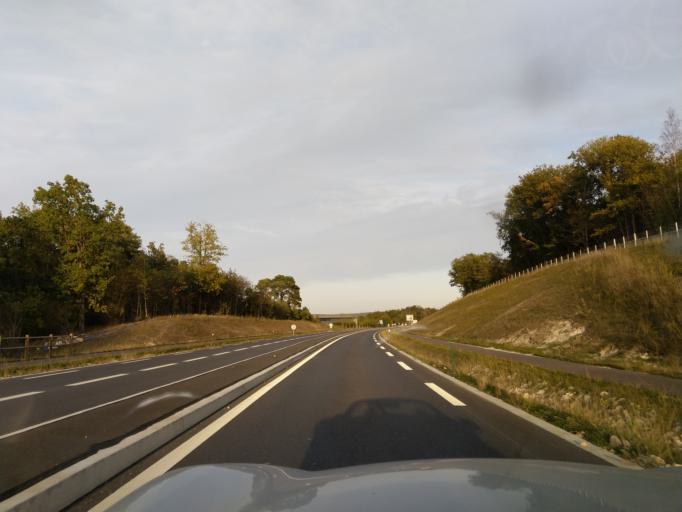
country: FR
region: Ile-de-France
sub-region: Departement de l'Essonne
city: Etampes
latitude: 48.4492
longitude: 2.1420
